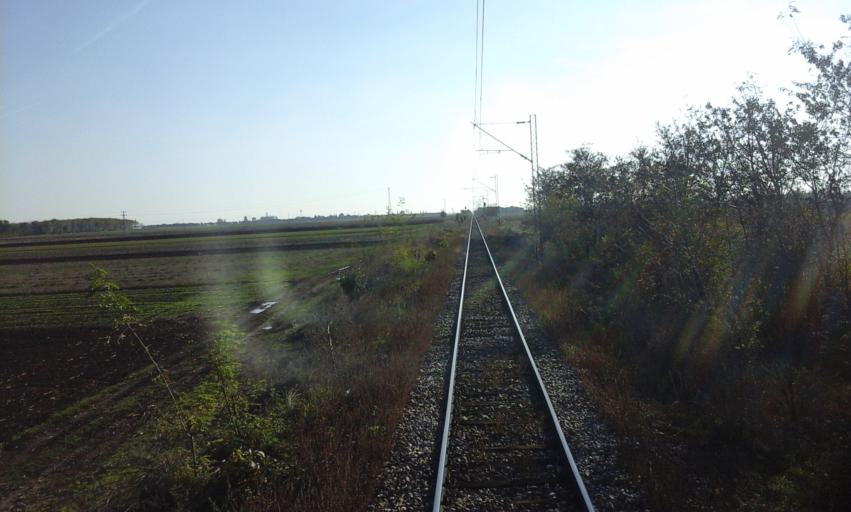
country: RS
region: Autonomna Pokrajina Vojvodina
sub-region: Severnobacki Okrug
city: Backa Topola
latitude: 45.7984
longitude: 19.6473
